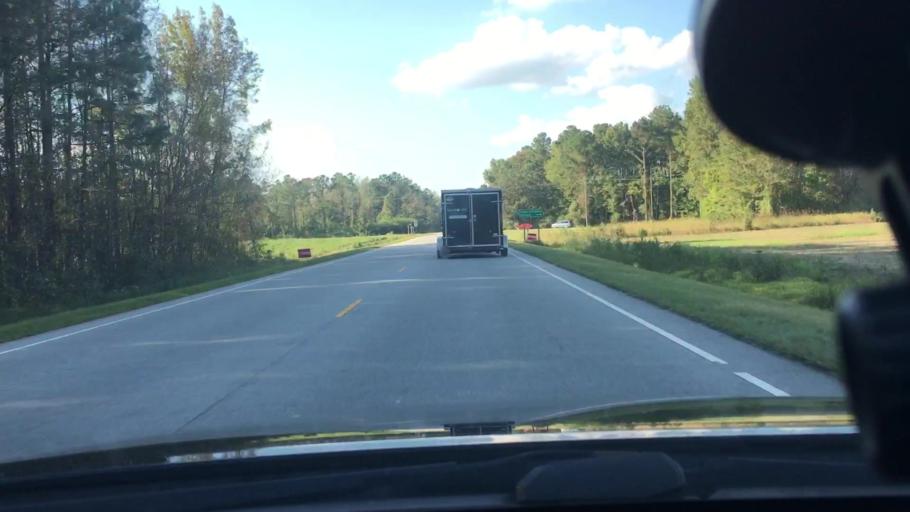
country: US
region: North Carolina
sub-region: Craven County
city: Vanceboro
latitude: 35.3079
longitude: -77.1369
